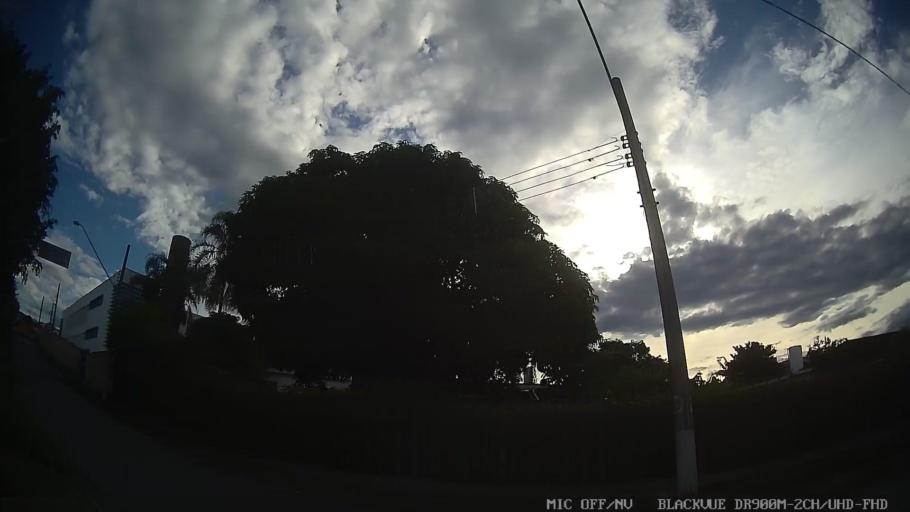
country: BR
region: Sao Paulo
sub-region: Mogi das Cruzes
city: Mogi das Cruzes
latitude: -23.5401
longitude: -46.2151
